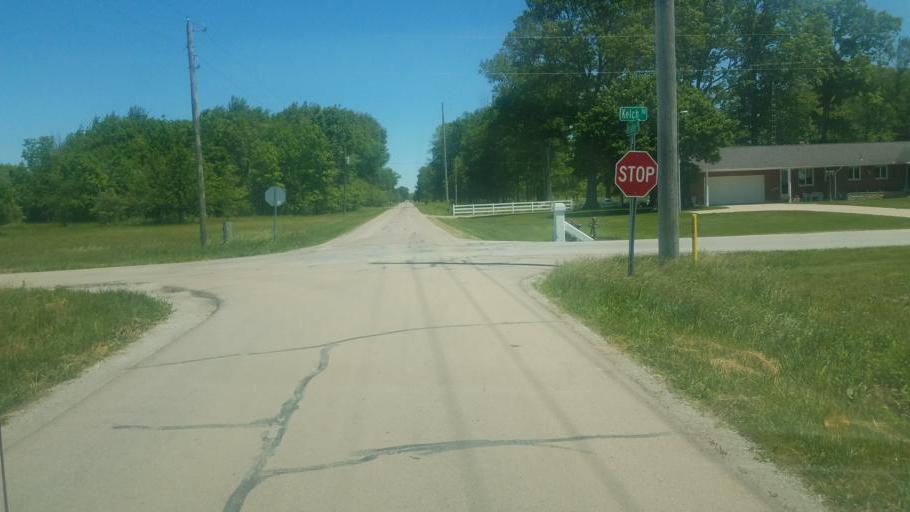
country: US
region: Ohio
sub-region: Darke County
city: Versailles
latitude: 40.2265
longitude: -84.3957
